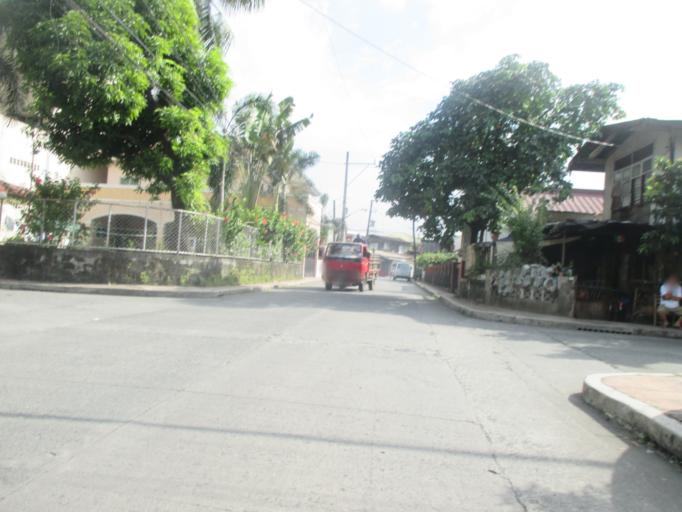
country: PH
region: Metro Manila
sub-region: Marikina
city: Calumpang
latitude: 14.6216
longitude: 121.0974
